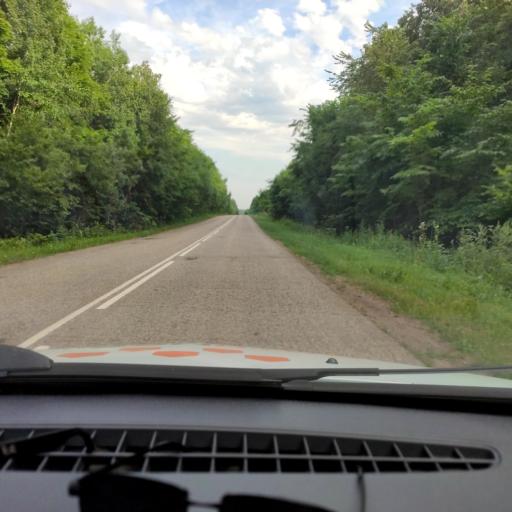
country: RU
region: Bashkortostan
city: Chishmy
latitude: 54.4525
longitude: 55.5465
